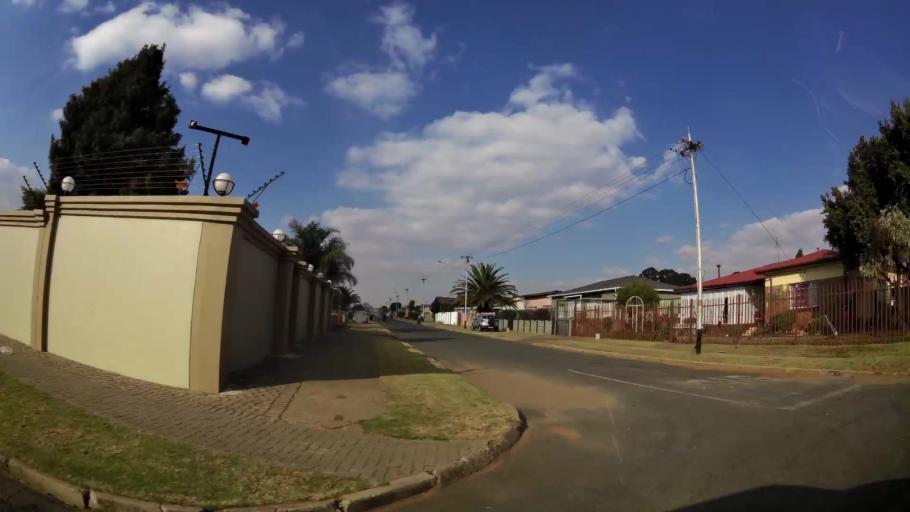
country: ZA
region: Gauteng
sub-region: West Rand District Municipality
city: Krugersdorp
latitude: -26.0937
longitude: 27.7439
